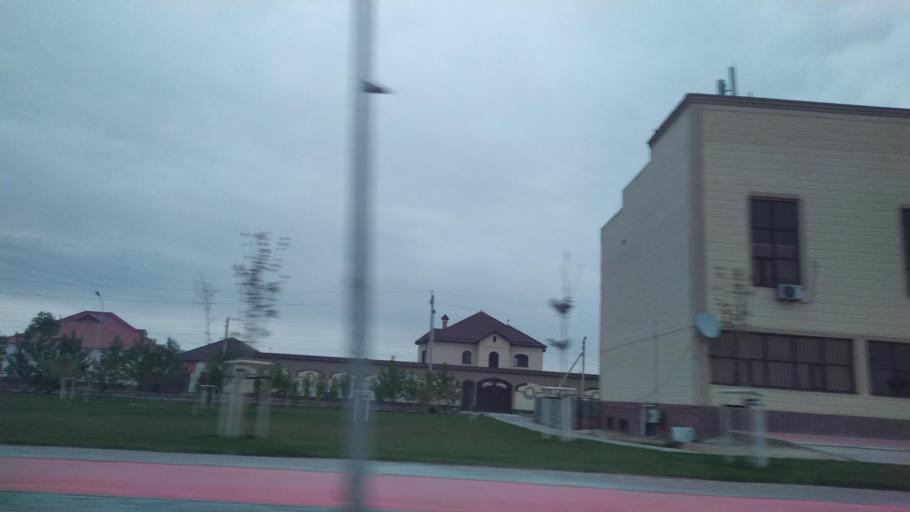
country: KZ
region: Ongtustik Qazaqstan
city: Turkestan
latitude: 43.2807
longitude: 68.3204
